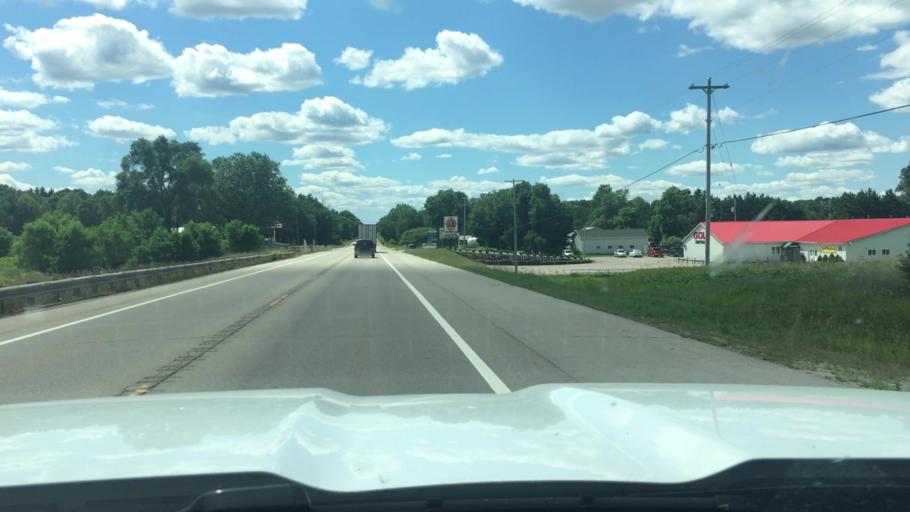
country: US
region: Michigan
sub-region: Montcalm County
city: Greenville
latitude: 43.1764
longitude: -85.3995
